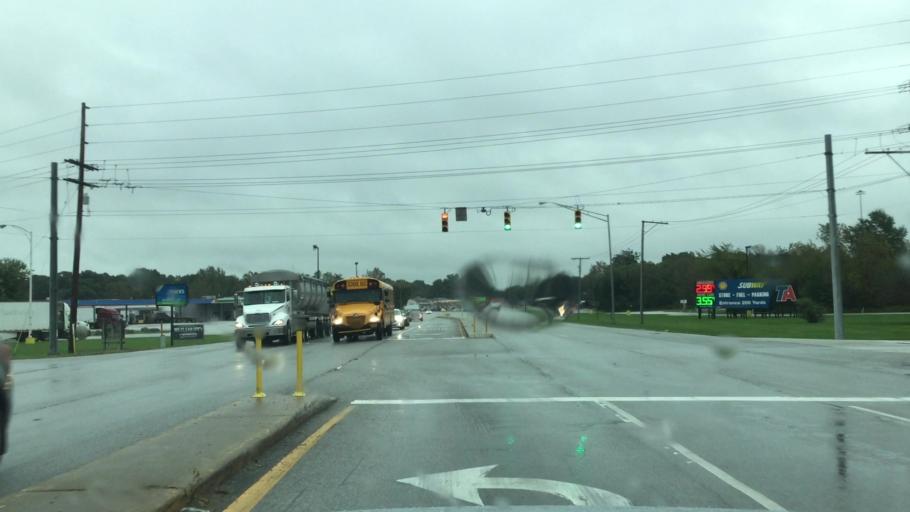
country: US
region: Indiana
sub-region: Porter County
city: Porter
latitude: 41.6105
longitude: -87.1009
